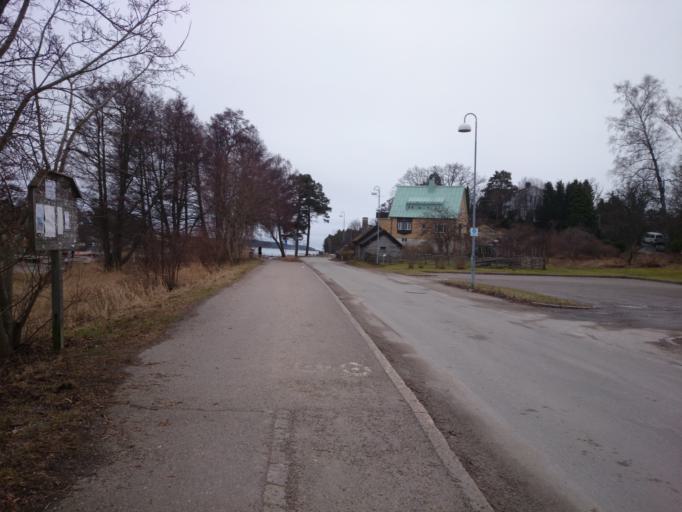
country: SE
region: Stockholm
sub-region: Nynashamns Kommun
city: Nynashamn
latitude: 58.8936
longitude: 17.9422
